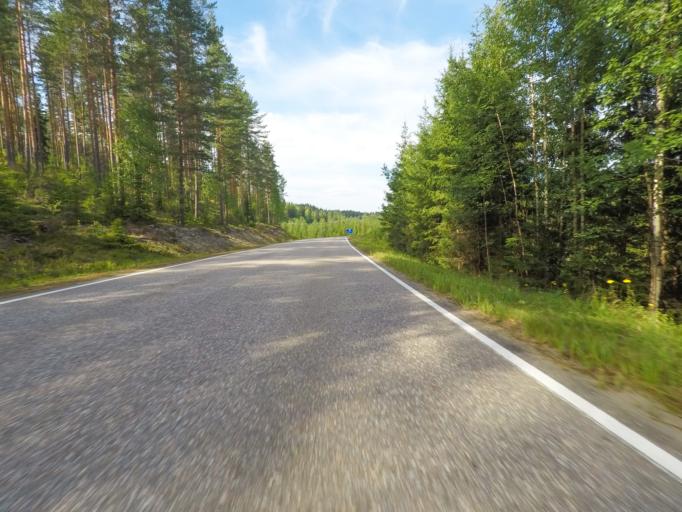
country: FI
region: Southern Savonia
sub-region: Savonlinna
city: Sulkava
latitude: 61.7241
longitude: 28.2056
